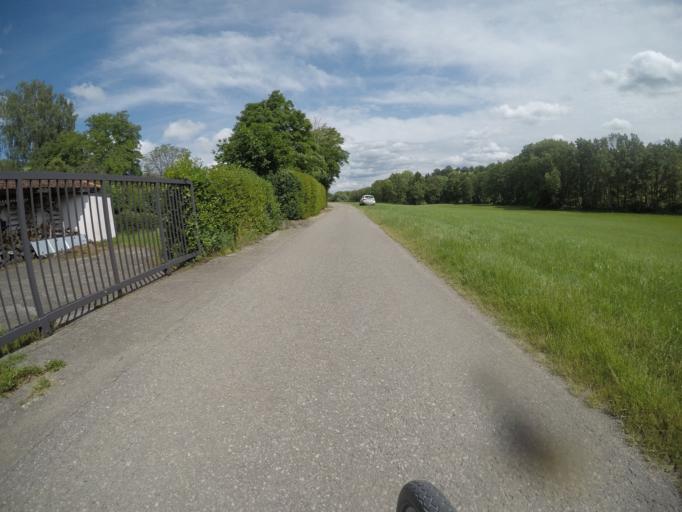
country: DE
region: Baden-Wuerttemberg
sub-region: Regierungsbezirk Stuttgart
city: Weil im Schonbuch
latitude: 48.6281
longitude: 9.0736
